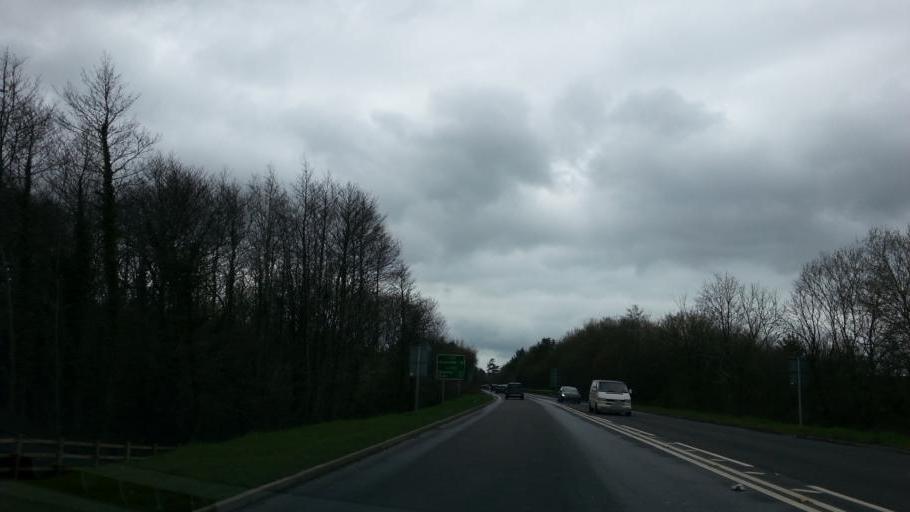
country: GB
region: England
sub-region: Devon
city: Barnstaple
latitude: 51.0712
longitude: -4.0324
